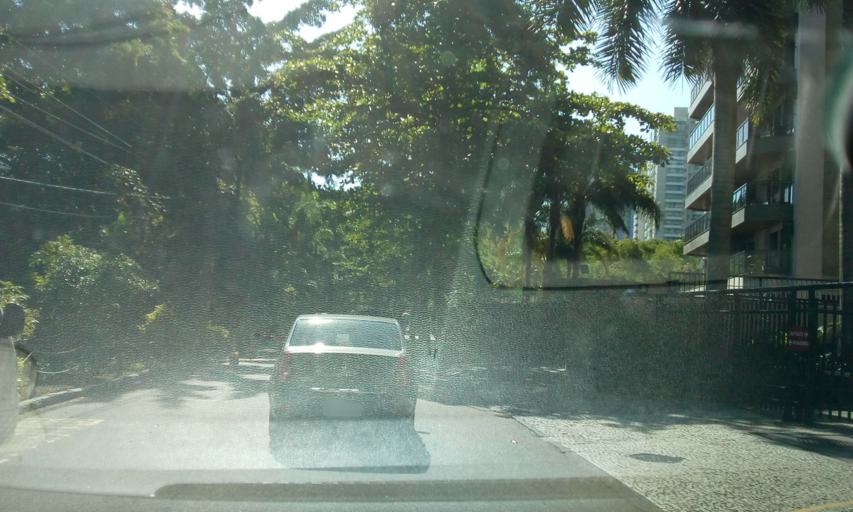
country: BR
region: Rio de Janeiro
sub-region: Rio De Janeiro
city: Rio de Janeiro
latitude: -23.0070
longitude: -43.3265
